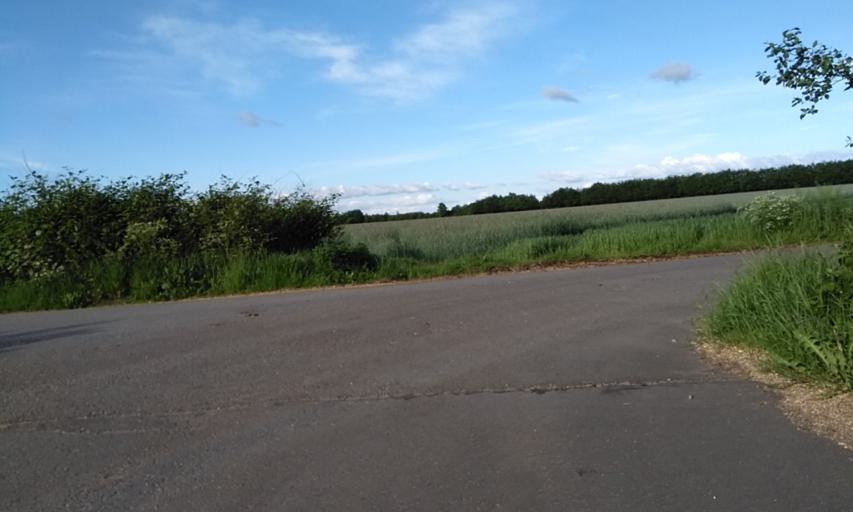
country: DE
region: Lower Saxony
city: Dollern
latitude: 53.5428
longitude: 9.5361
